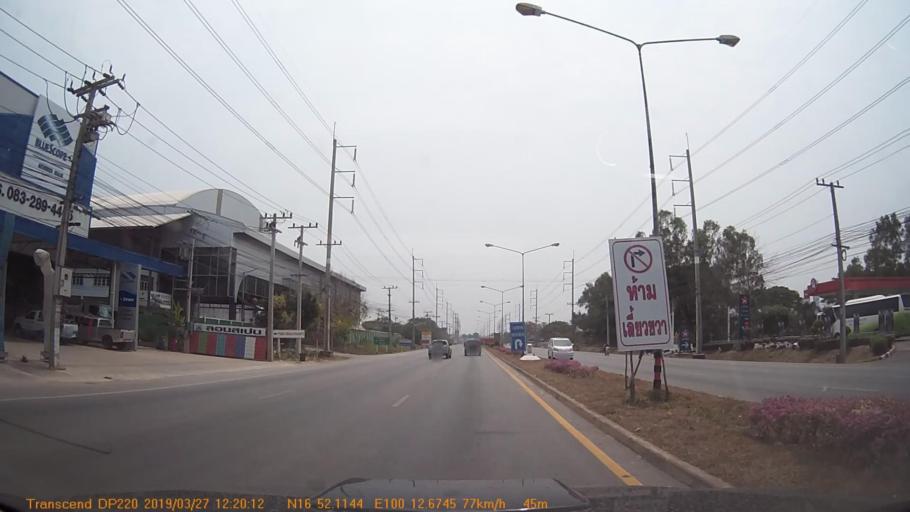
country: TH
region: Phitsanulok
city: Phitsanulok
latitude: 16.8684
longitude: 100.2114
